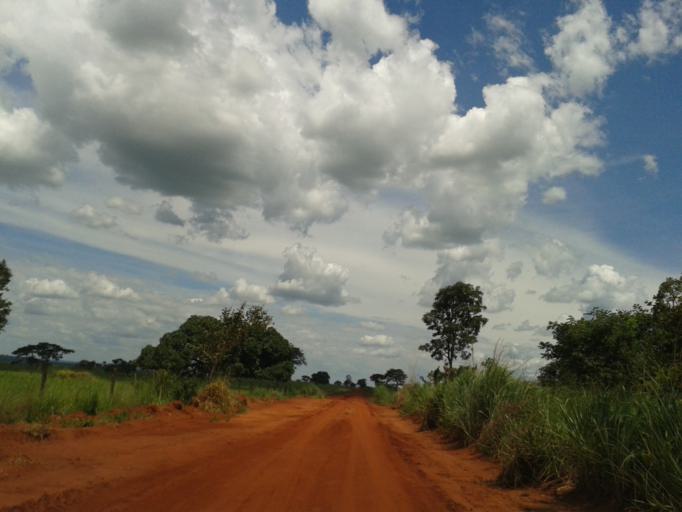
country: BR
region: Minas Gerais
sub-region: Ituiutaba
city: Ituiutaba
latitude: -18.8879
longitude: -49.4689
